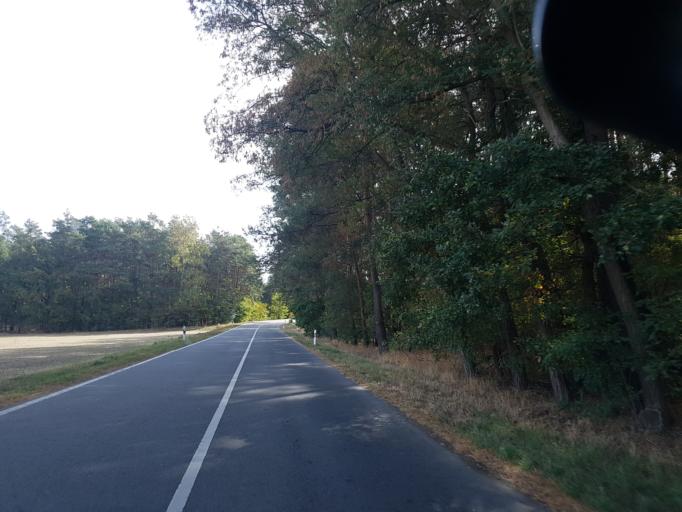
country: DE
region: Brandenburg
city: Schlieben
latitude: 51.6953
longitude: 13.4291
